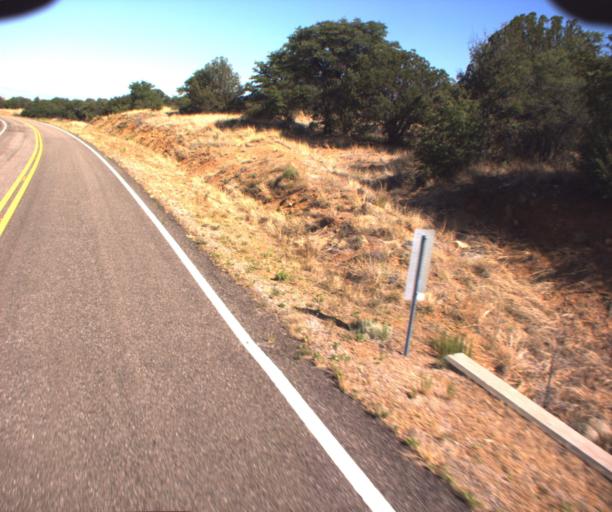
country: US
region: Arizona
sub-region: Graham County
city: Swift Trail Junction
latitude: 32.5967
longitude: -109.8614
